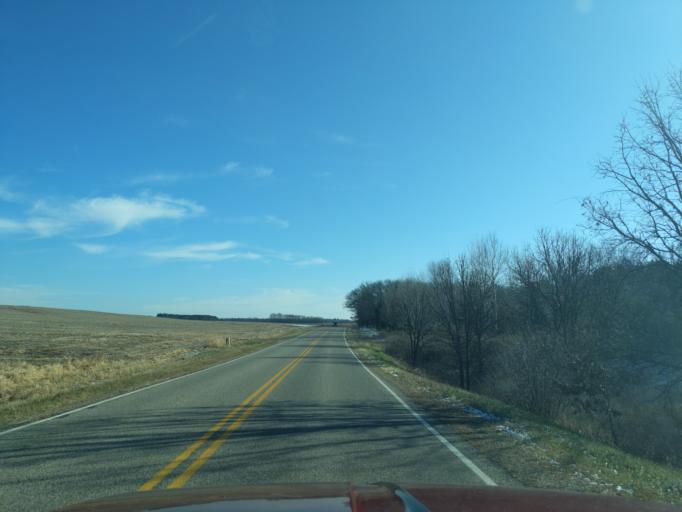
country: US
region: Wisconsin
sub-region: Waushara County
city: Silver Lake
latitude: 44.0927
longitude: -89.1847
